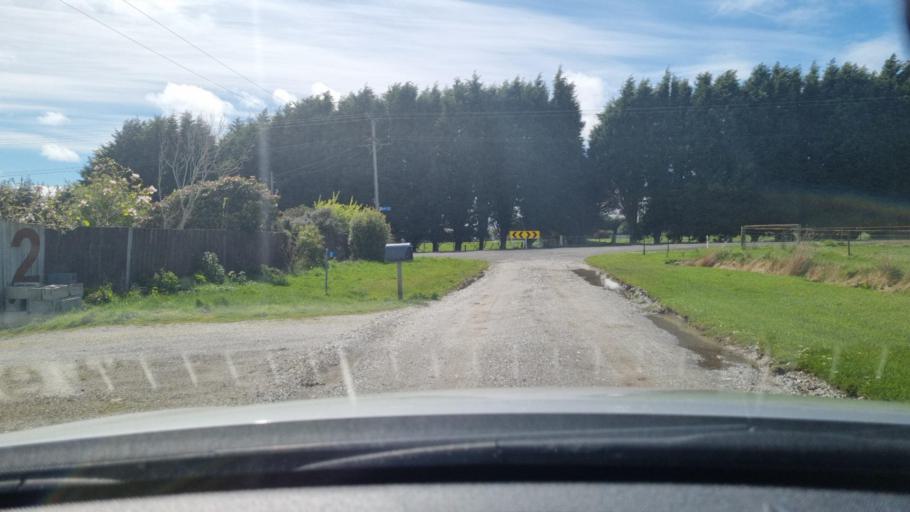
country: NZ
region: Southland
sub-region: Invercargill City
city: Invercargill
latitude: -46.4760
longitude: 168.3913
